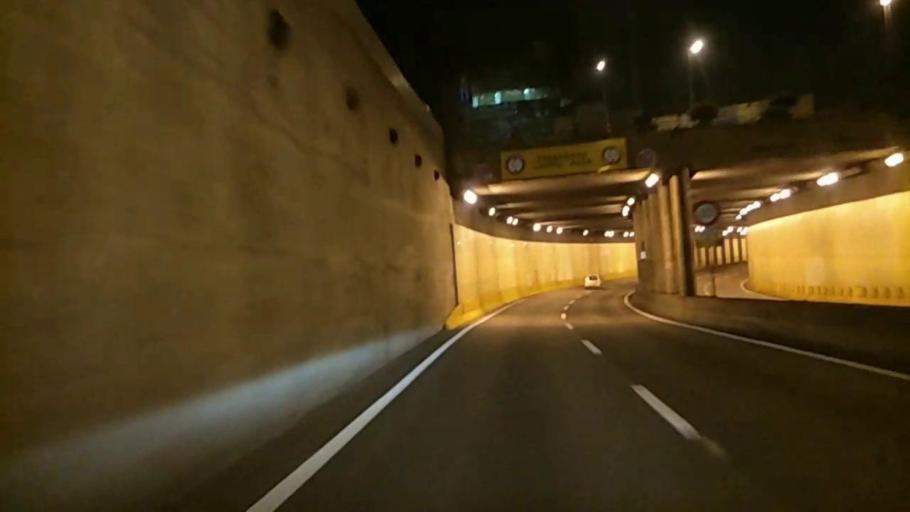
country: MY
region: Selangor
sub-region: Petaling
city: Petaling Jaya
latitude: 3.1328
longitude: 101.6251
